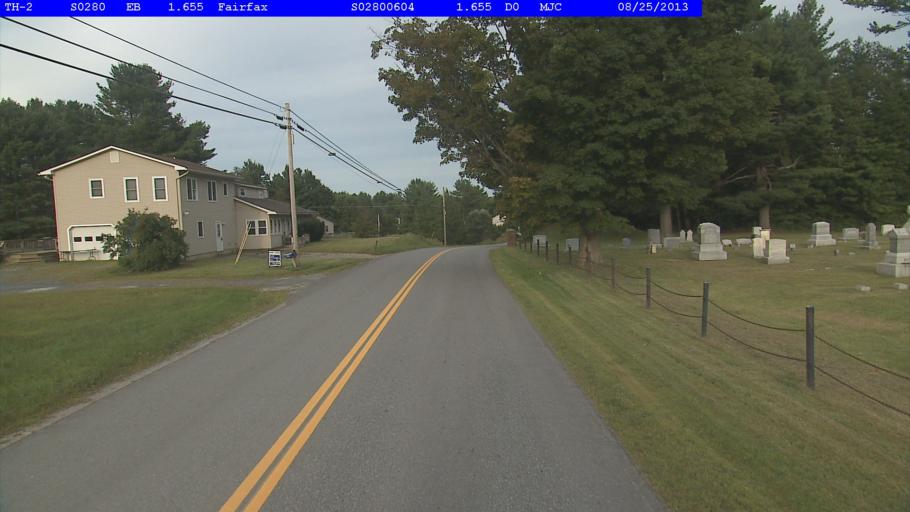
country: US
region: Vermont
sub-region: Chittenden County
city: Milton
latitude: 44.6713
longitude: -72.9788
